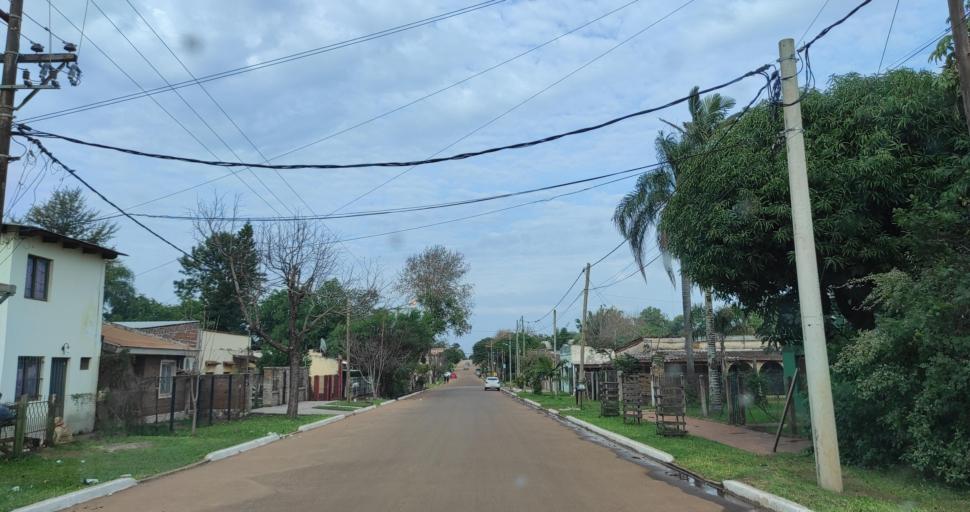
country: AR
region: Corrientes
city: Santo Tome
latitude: -28.5528
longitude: -56.0372
